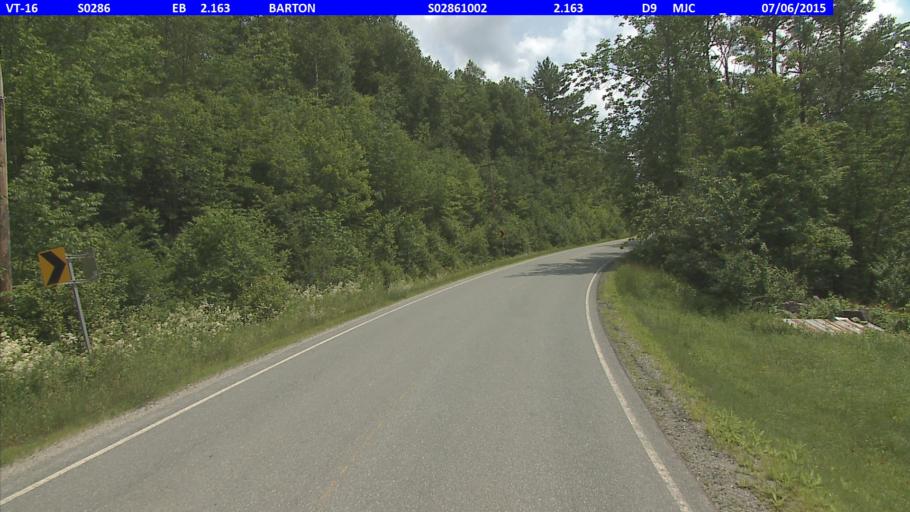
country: US
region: Vermont
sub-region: Orleans County
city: Newport
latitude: 44.7642
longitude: -72.1430
